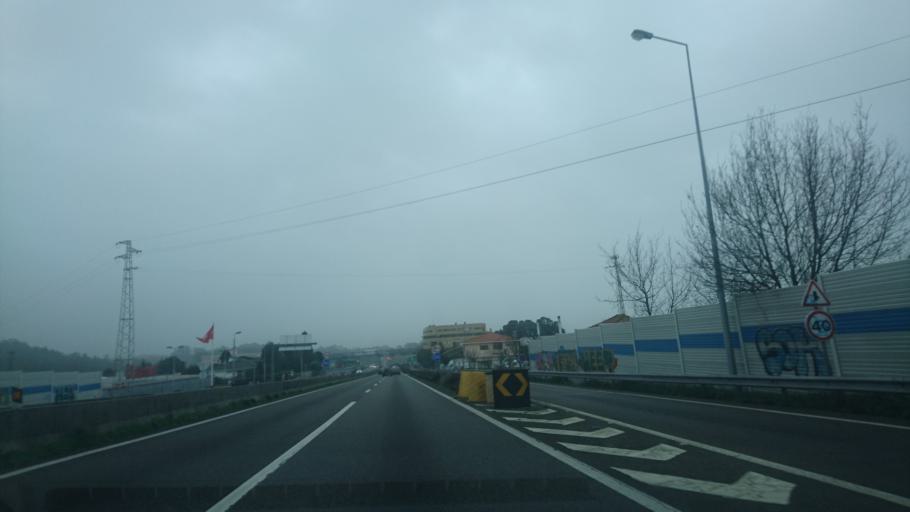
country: PT
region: Porto
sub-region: Vila Nova de Gaia
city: Vilar do Paraiso
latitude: 41.0971
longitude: -8.6278
